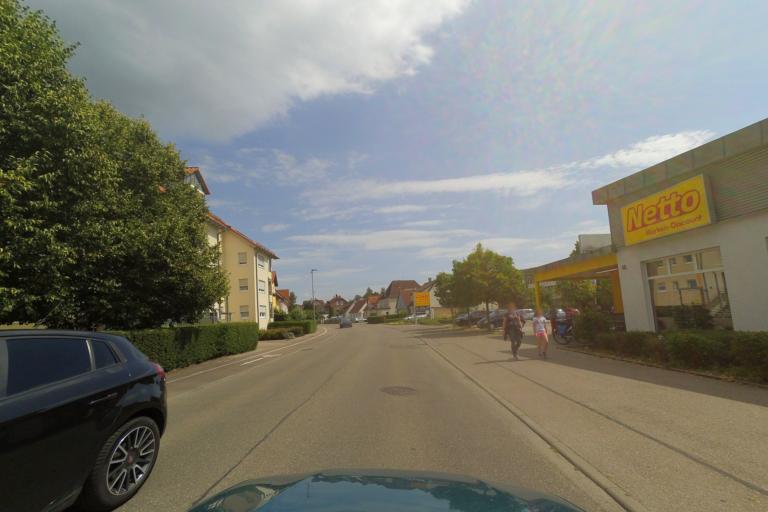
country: DE
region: Baden-Wuerttemberg
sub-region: Regierungsbezirk Stuttgart
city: Aalen
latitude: 48.8359
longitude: 10.0997
